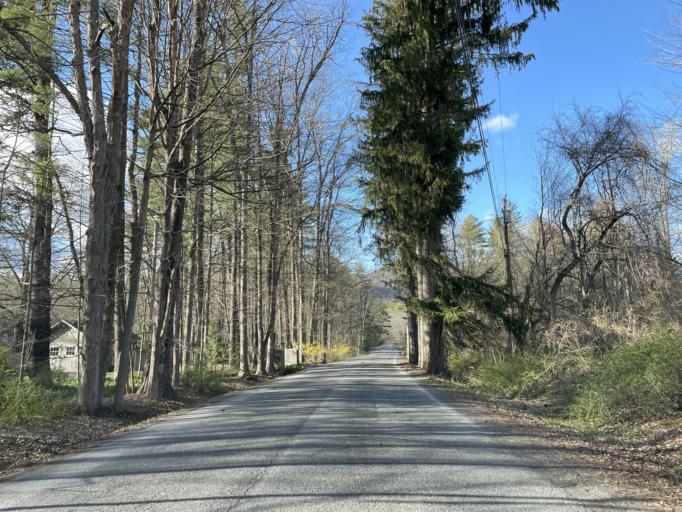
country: US
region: New York
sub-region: Ulster County
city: Woodstock
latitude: 42.0421
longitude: -74.1408
